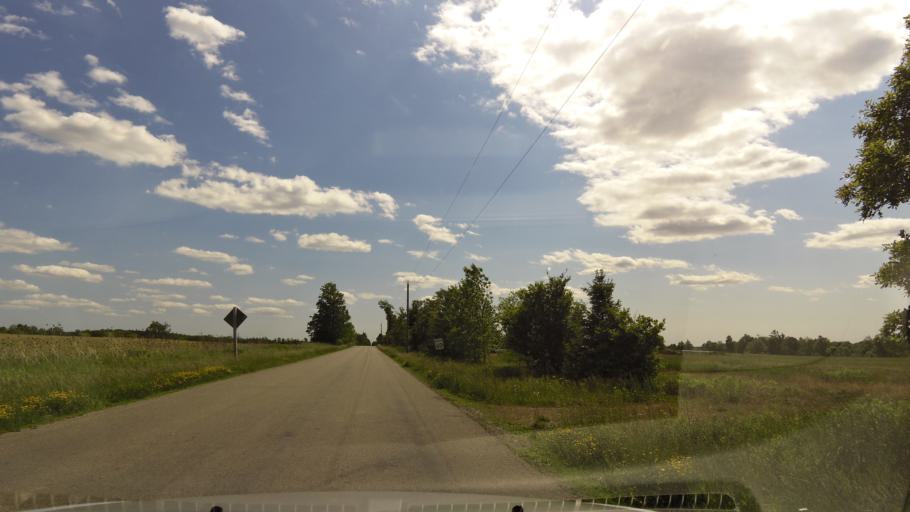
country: CA
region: Ontario
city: Ancaster
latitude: 43.1432
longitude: -80.0749
